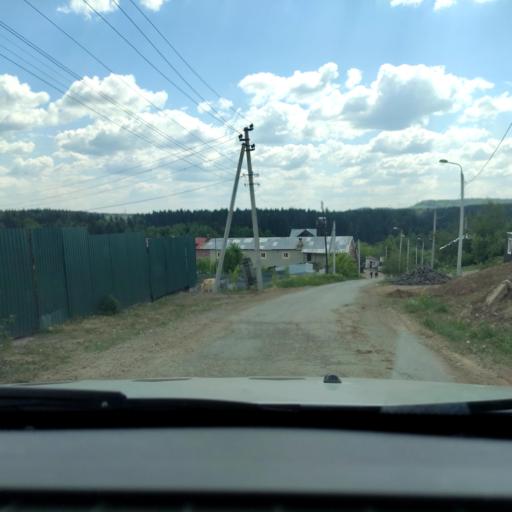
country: RU
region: Perm
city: Perm
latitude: 57.9927
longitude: 56.3380
